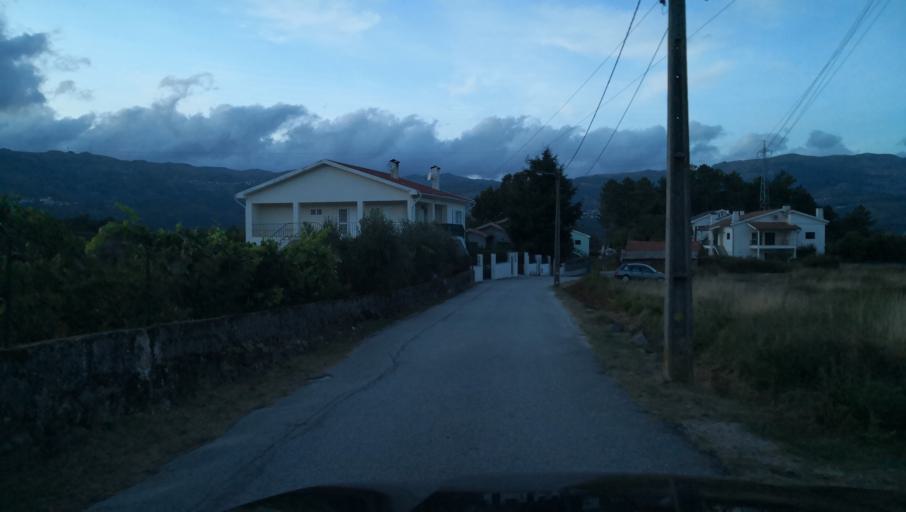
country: PT
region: Vila Real
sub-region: Vila Real
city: Vila Real
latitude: 41.2857
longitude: -7.7647
